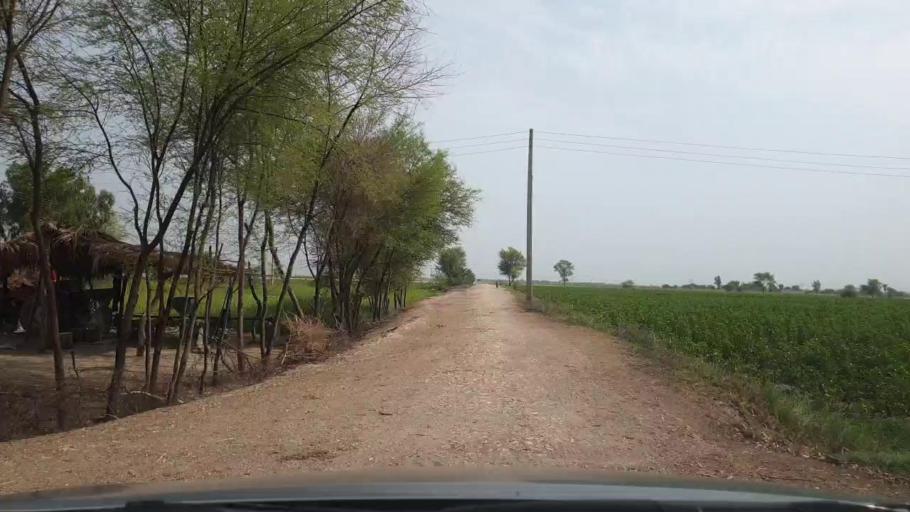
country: PK
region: Sindh
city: Rohri
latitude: 27.6582
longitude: 69.0245
